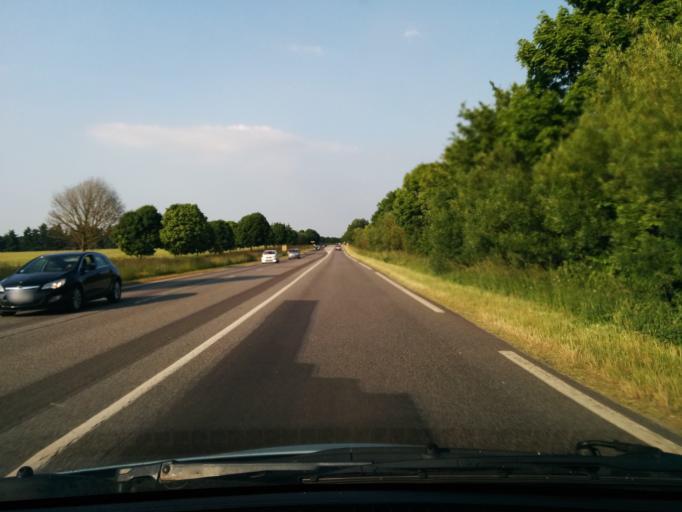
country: FR
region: Haute-Normandie
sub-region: Departement de l'Eure
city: Saint-Marcel
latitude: 49.0728
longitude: 1.4317
